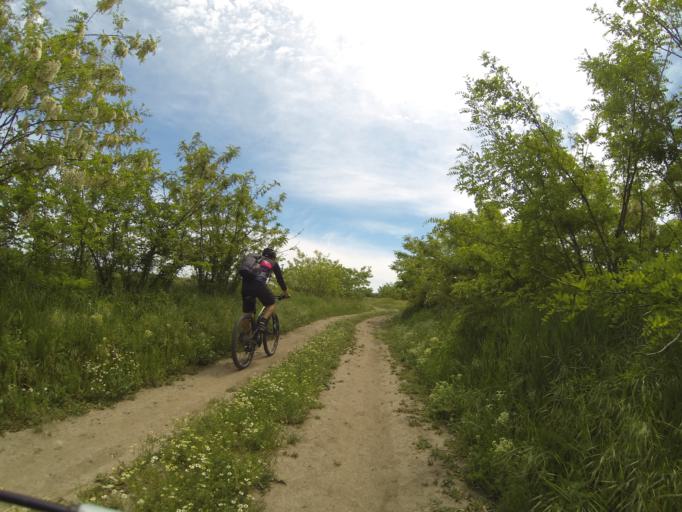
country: RO
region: Dolj
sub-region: Comuna Leu
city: Leu
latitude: 44.2009
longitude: 23.9994
